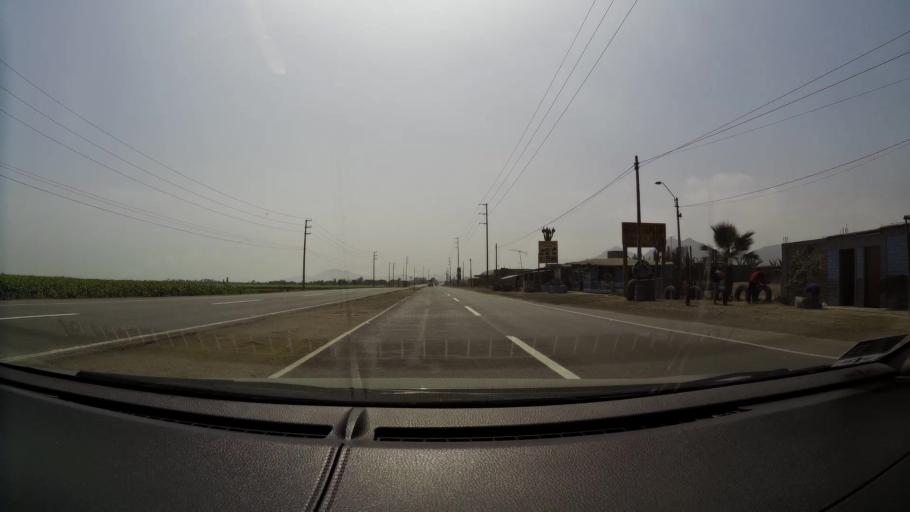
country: PE
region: Lima
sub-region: Provincia de Huaral
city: Chancay
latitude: -11.5398
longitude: -77.2819
